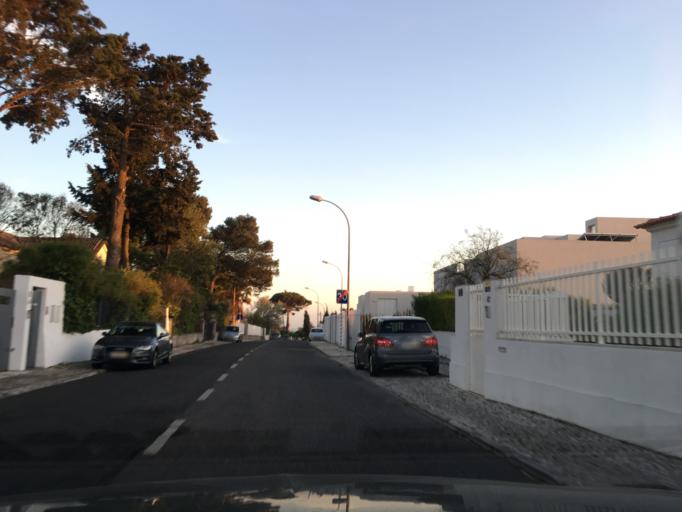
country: PT
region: Lisbon
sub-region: Oeiras
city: Terrugem
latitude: 38.7024
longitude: -9.2884
